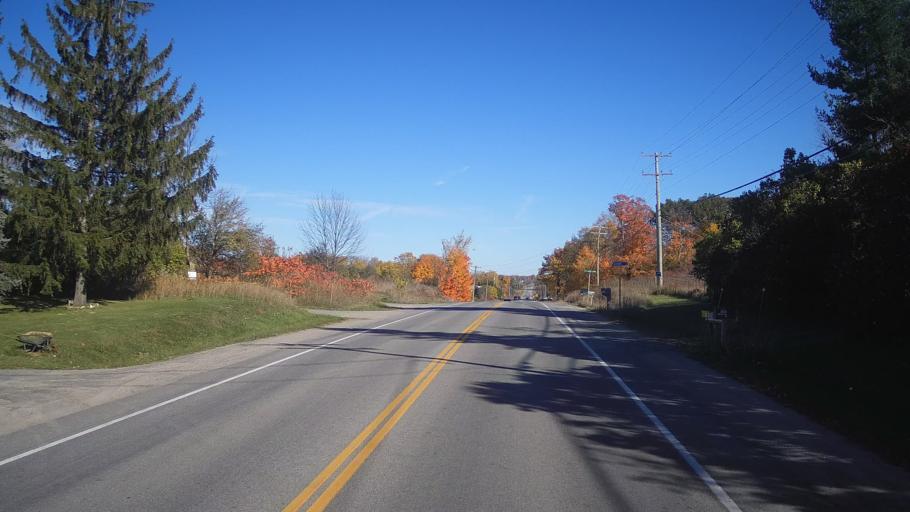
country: CA
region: Ontario
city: Kingston
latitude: 44.4073
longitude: -76.5789
